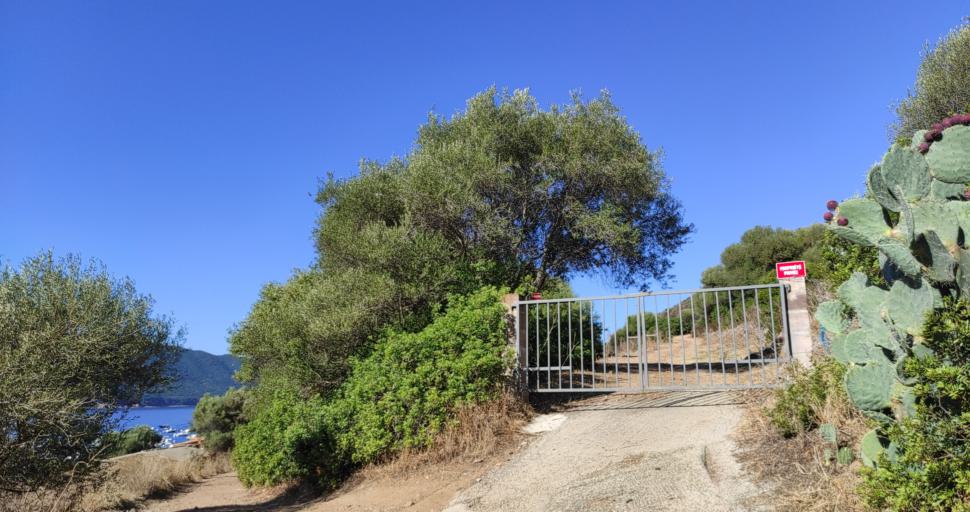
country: FR
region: Corsica
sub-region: Departement de la Corse-du-Sud
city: Alata
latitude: 41.9949
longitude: 8.6671
